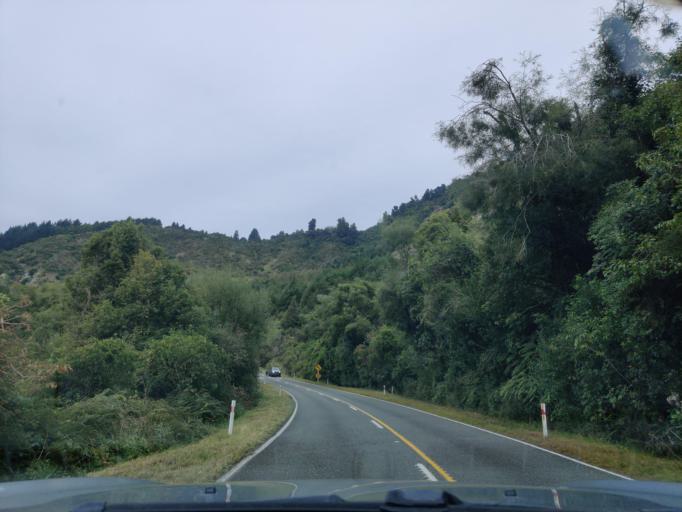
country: NZ
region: West Coast
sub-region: Buller District
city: Westport
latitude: -41.8444
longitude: 171.9109
